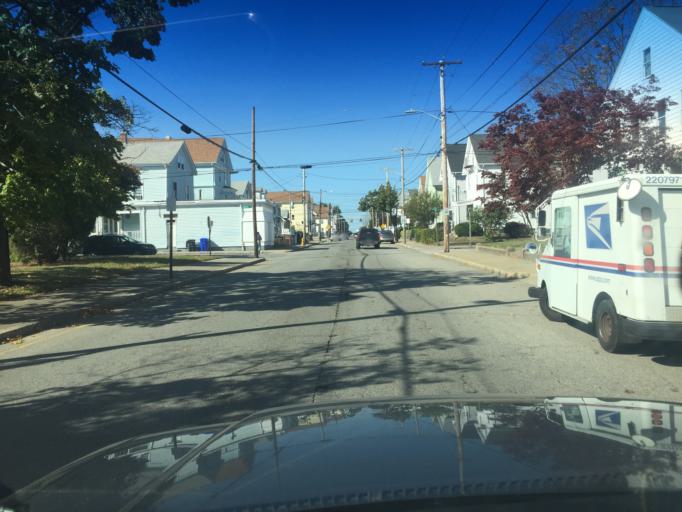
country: US
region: Rhode Island
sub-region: Providence County
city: Pawtucket
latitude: 41.8672
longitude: -71.3750
